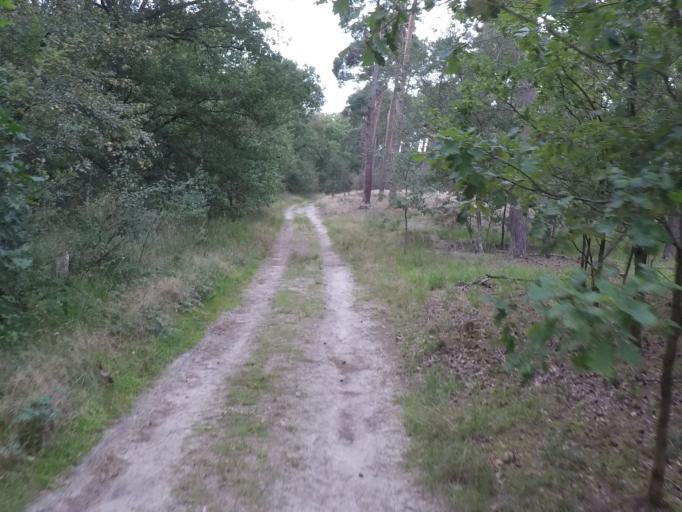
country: BE
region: Flanders
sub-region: Provincie Antwerpen
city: Herentals
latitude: 51.1943
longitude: 4.8653
